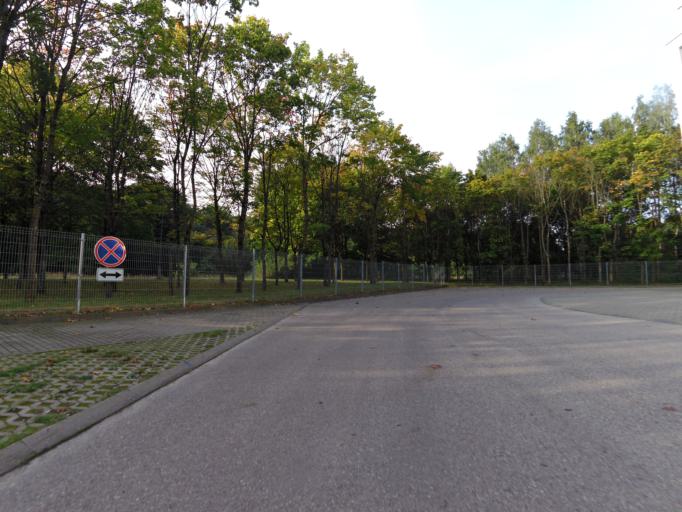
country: LT
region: Vilnius County
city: Lazdynai
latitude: 54.6799
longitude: 25.2247
